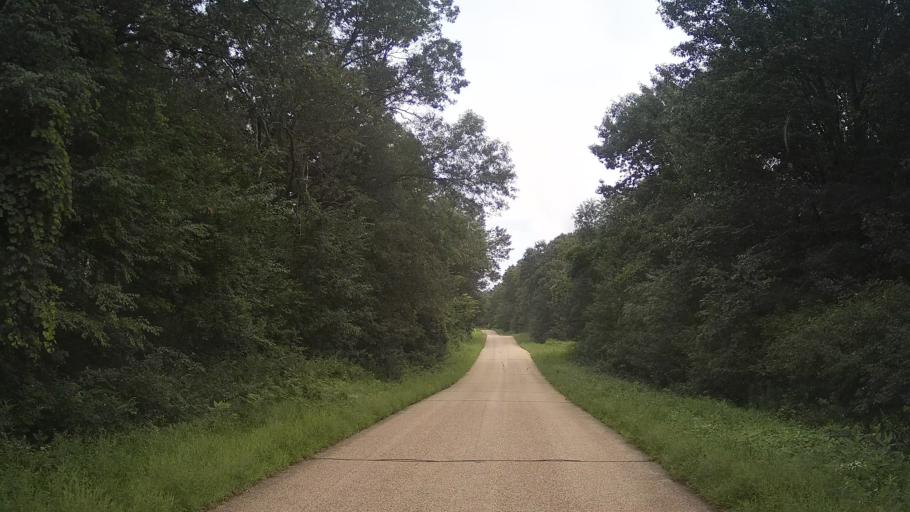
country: US
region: Wisconsin
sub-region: Adams County
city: Friendship
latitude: 44.0271
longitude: -89.9115
